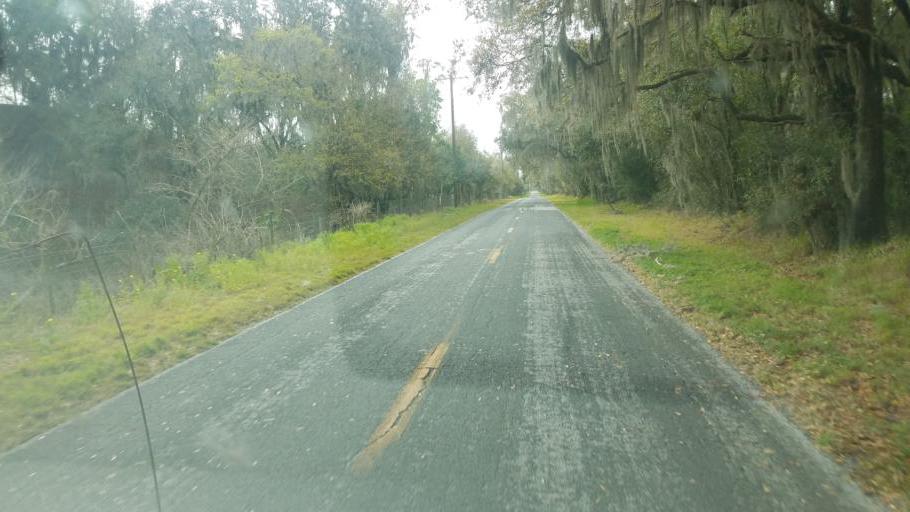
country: US
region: Florida
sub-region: Polk County
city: Willow Oak
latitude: 27.8966
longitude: -82.1043
